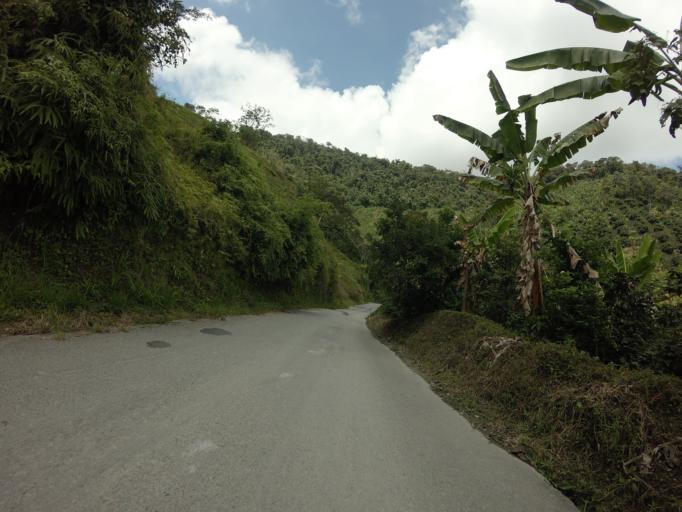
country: CO
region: Caldas
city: Marquetalia
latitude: 5.2940
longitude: -75.0902
